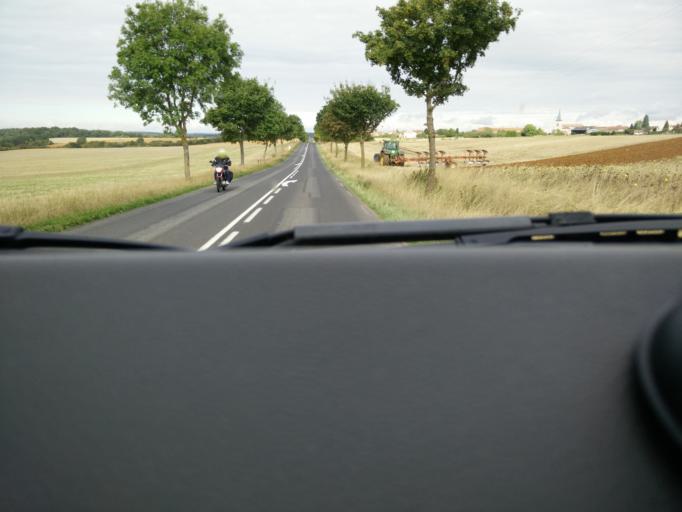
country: FR
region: Lorraine
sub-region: Departement de Meurthe-et-Moselle
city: Montauville
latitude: 48.8979
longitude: 5.9681
